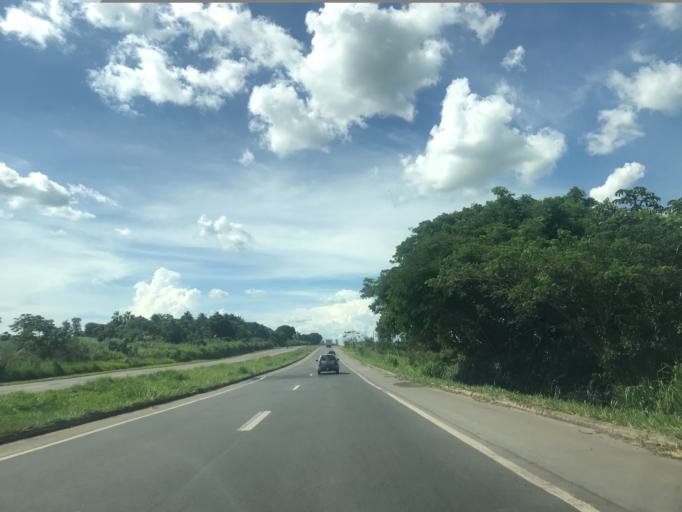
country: BR
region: Goias
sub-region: Morrinhos
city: Morrinhos
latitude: -17.5341
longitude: -49.2130
